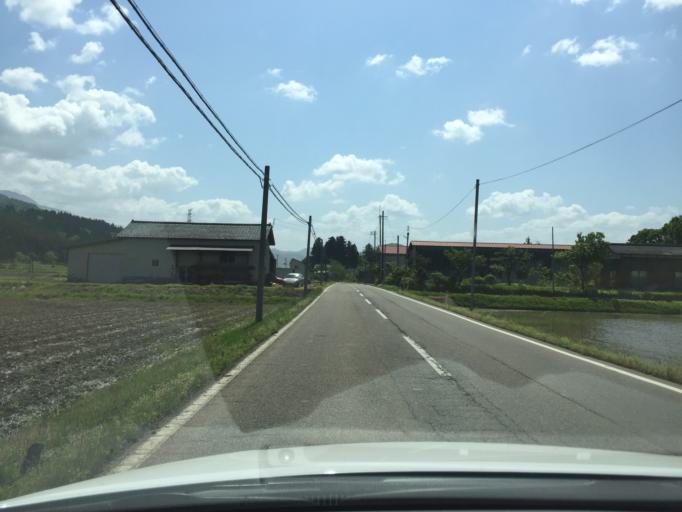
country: JP
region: Niigata
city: Tochio-honcho
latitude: 37.5507
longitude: 139.0842
